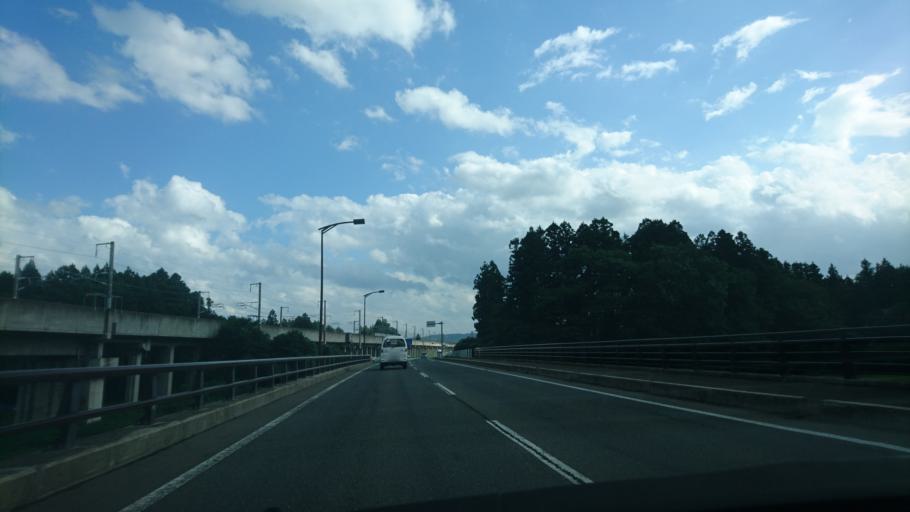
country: JP
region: Iwate
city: Hanamaki
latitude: 39.4554
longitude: 141.1753
